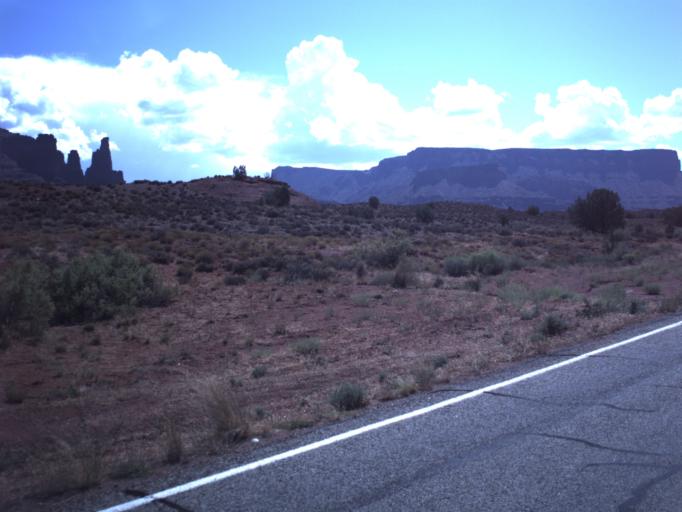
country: US
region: Utah
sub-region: Grand County
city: Moab
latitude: 38.7461
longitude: -109.3305
